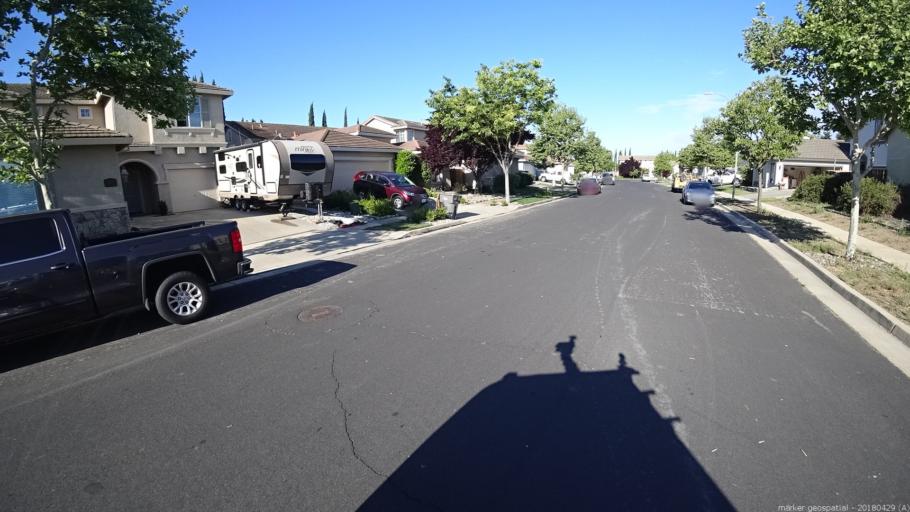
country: US
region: California
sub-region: Yolo County
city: West Sacramento
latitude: 38.5393
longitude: -121.5741
